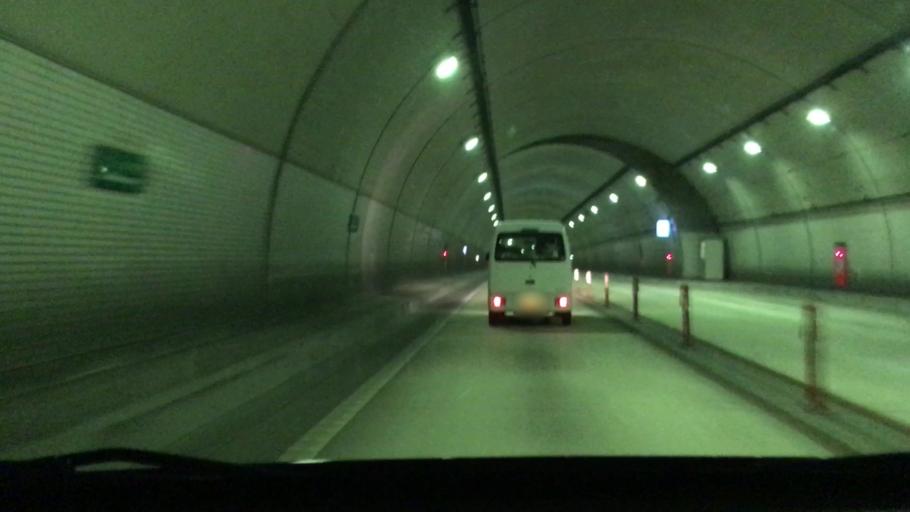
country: JP
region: Nagasaki
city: Sasebo
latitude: 33.0911
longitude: 129.7785
